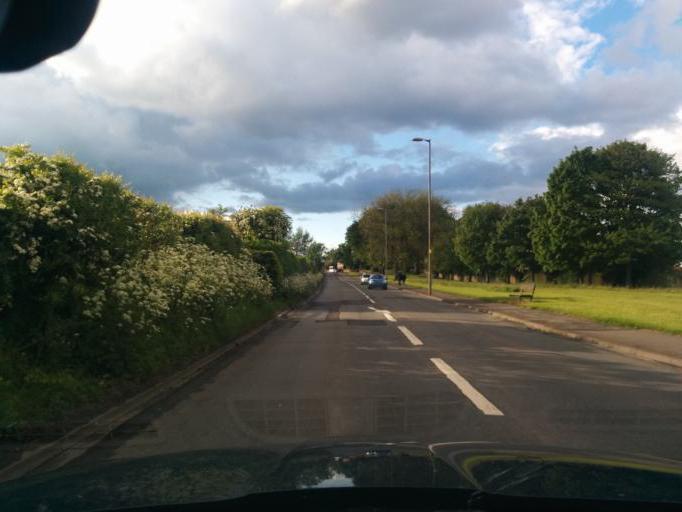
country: GB
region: England
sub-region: Northumberland
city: Choppington
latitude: 55.1534
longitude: -1.6034
